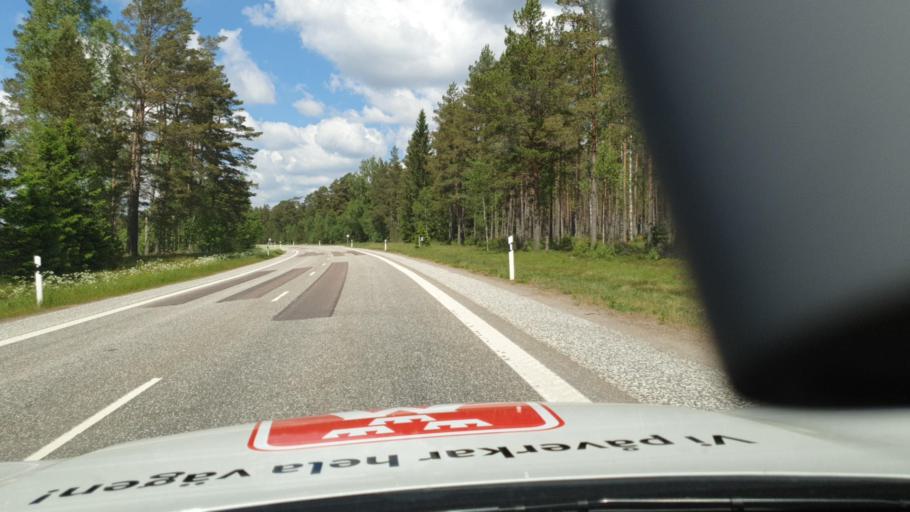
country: SE
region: Joenkoeping
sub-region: Jonkopings Kommun
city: Odensjo
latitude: 57.6383
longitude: 14.2049
